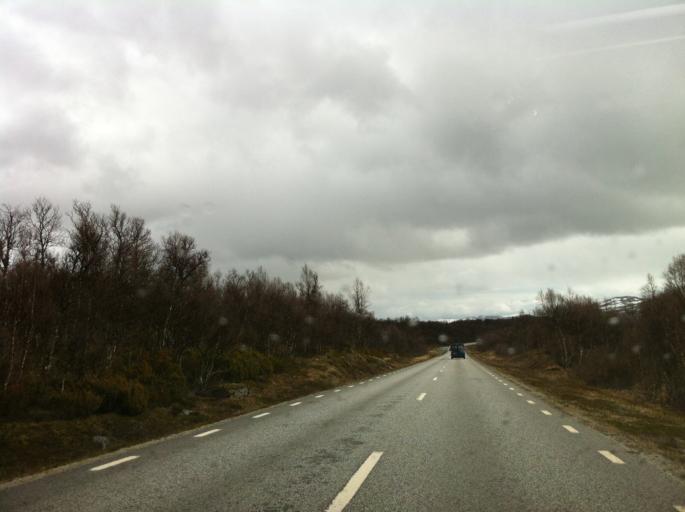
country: NO
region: Sor-Trondelag
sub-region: Tydal
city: Aas
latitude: 62.6367
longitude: 12.1076
